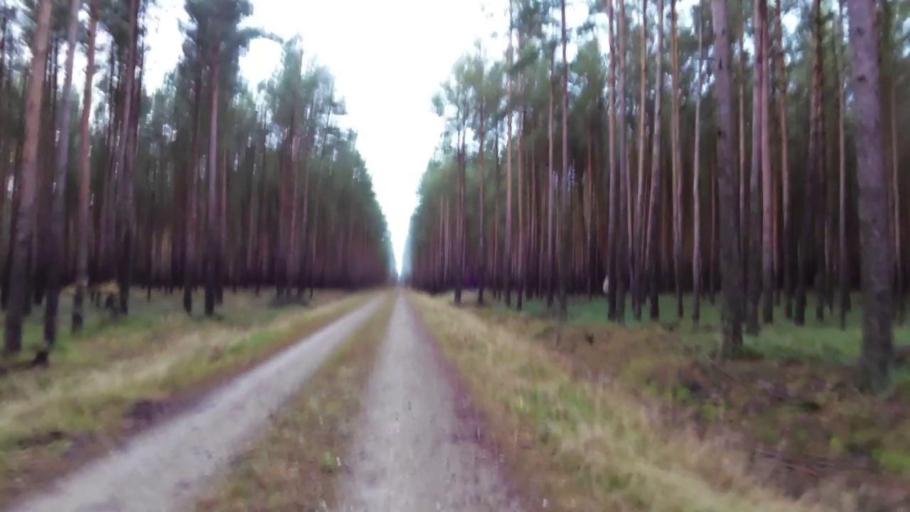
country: PL
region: West Pomeranian Voivodeship
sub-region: Powiat goleniowski
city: Stepnica
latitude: 53.6342
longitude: 14.7141
